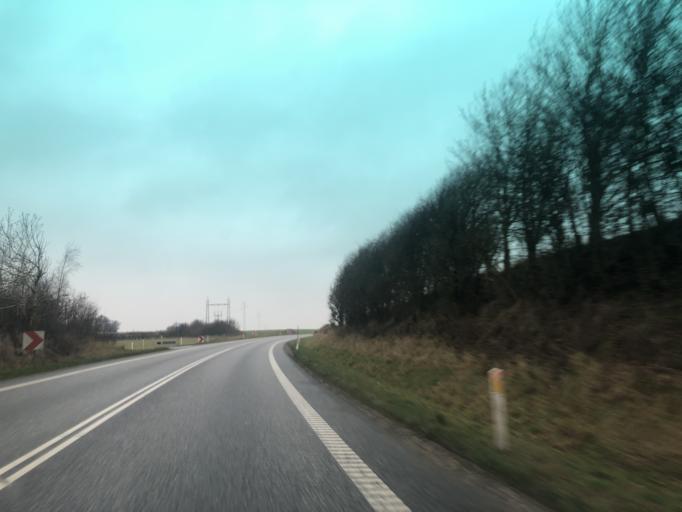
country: DK
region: Central Jutland
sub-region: Struer Kommune
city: Struer
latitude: 56.5083
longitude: 8.5700
